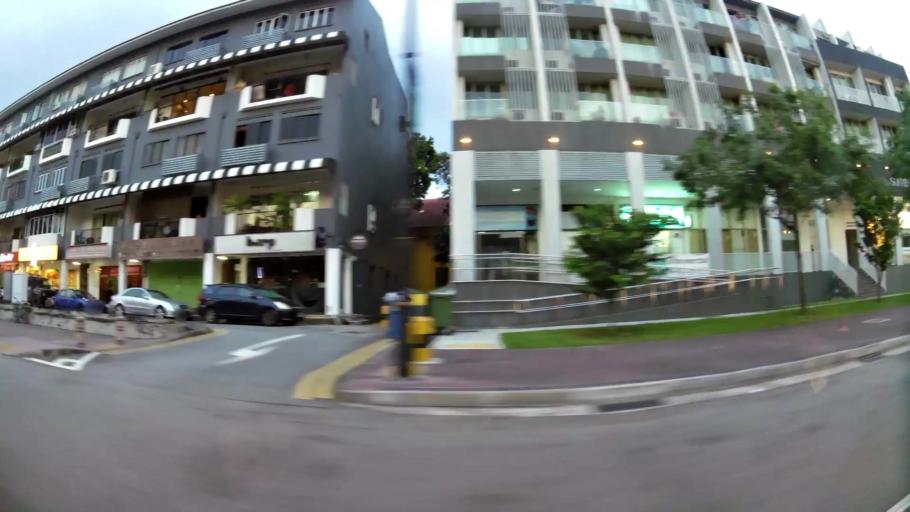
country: SG
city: Singapore
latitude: 1.3078
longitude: 103.8954
